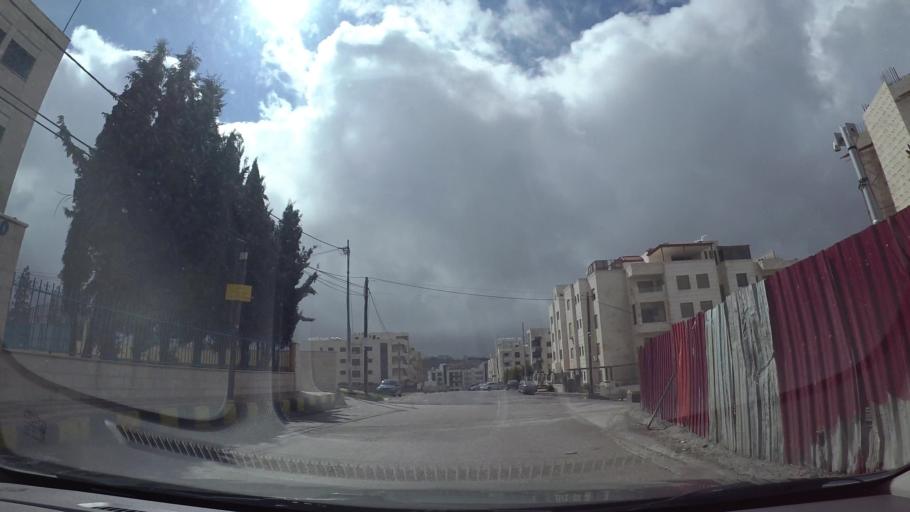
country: JO
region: Amman
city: Wadi as Sir
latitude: 31.9402
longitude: 35.8537
